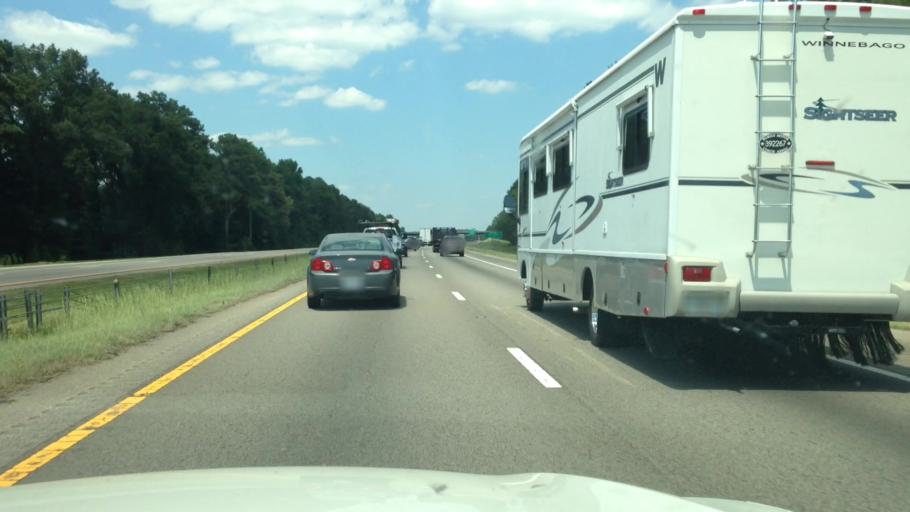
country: US
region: North Carolina
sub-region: Cumberland County
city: Hope Mills
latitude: 34.9161
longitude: -78.9511
